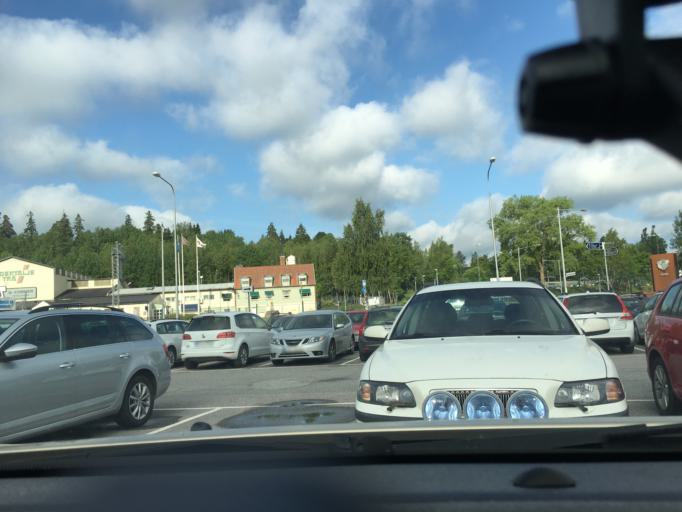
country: SE
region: Stockholm
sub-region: Sodertalje Kommun
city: Pershagen
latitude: 59.1651
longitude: 17.6416
